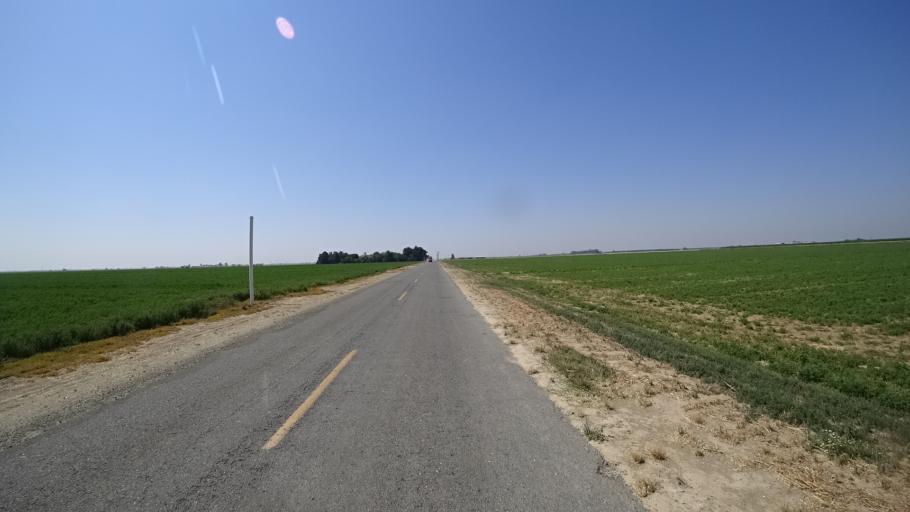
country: US
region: California
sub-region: Tulare County
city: Goshen
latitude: 36.3912
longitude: -119.5289
